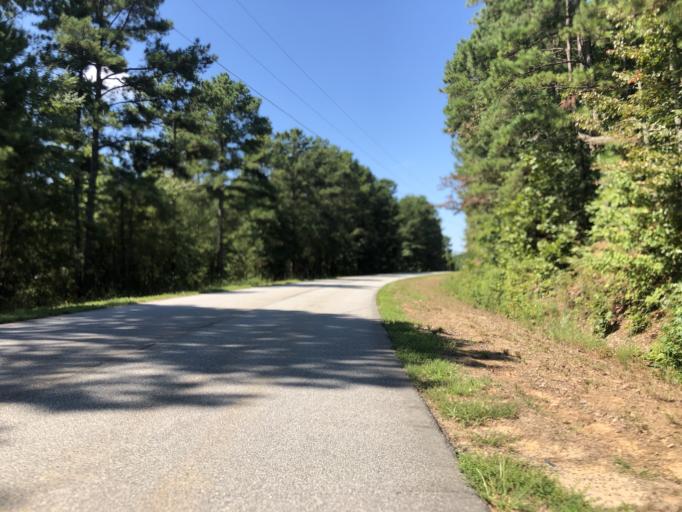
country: US
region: Georgia
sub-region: Heard County
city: Franklin
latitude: 33.3832
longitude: -85.0036
